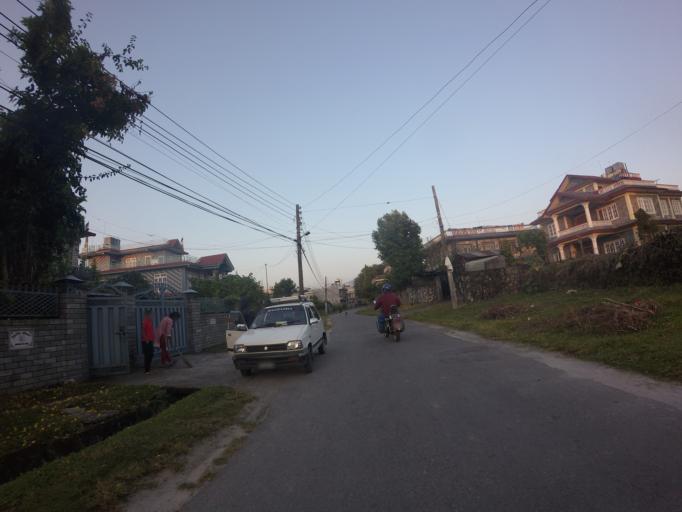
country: NP
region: Western Region
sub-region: Gandaki Zone
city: Pokhara
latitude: 28.2089
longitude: 83.9956
